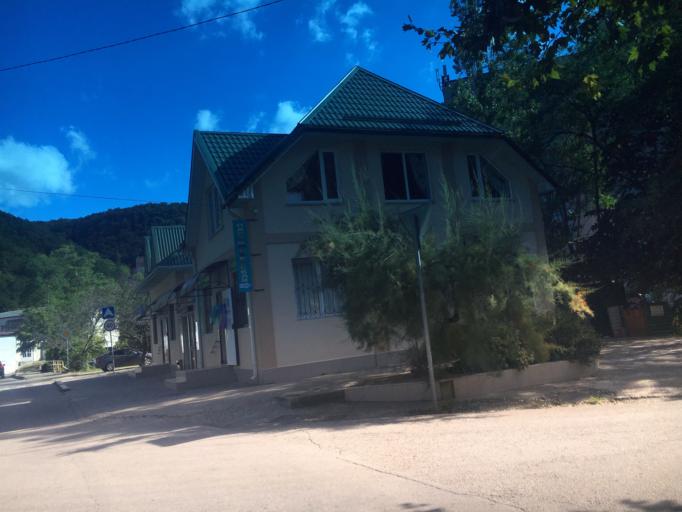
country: RU
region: Krasnodarskiy
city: Nebug
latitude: 44.1800
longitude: 38.9743
